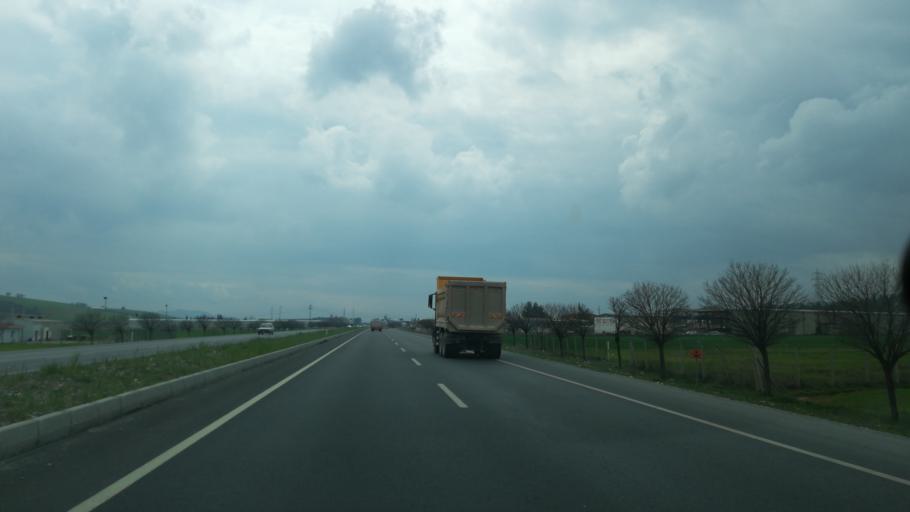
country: TR
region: Kahramanmaras
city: Turkoglu
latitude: 37.4333
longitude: 36.8850
